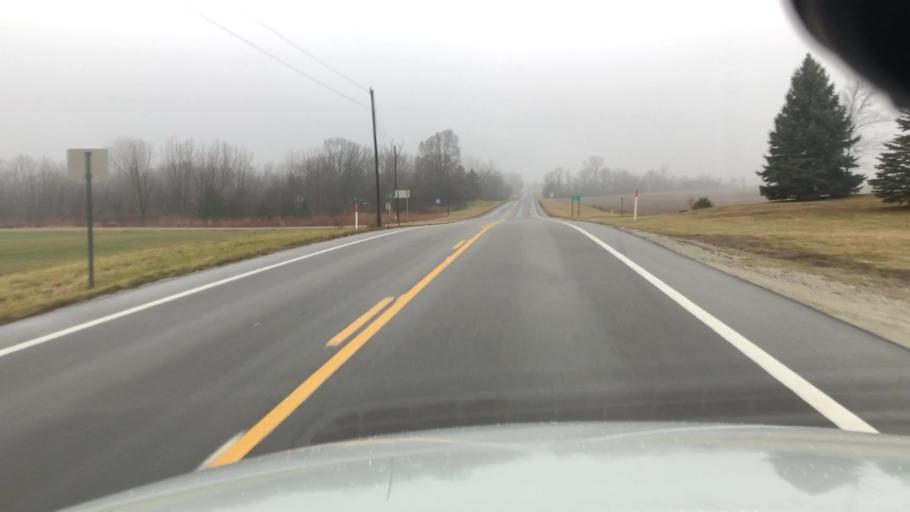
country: US
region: Ohio
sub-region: Logan County
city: Lakeview
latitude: 40.6441
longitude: -83.9293
